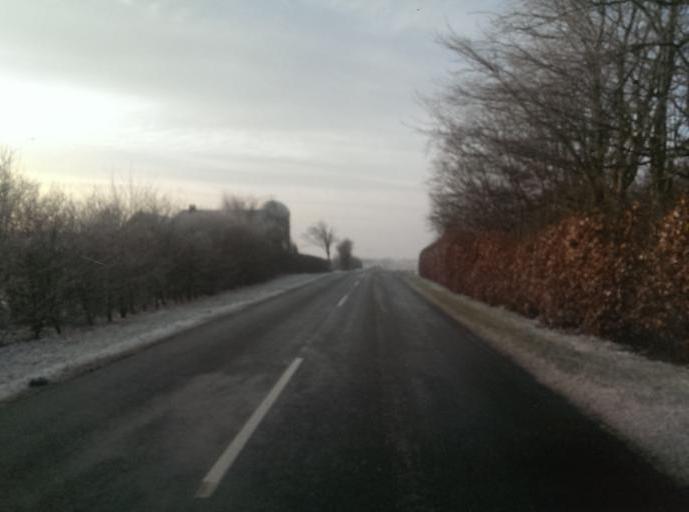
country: DK
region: South Denmark
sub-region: Esbjerg Kommune
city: Tjaereborg
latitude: 55.4589
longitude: 8.6292
